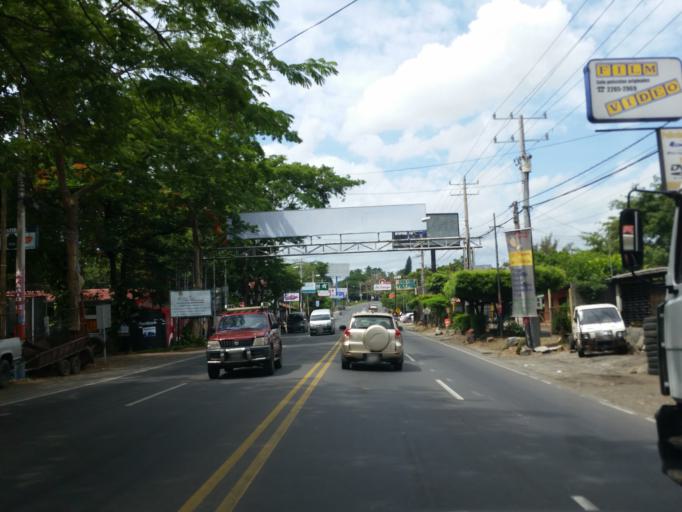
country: NI
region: Managua
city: Ciudad Sandino
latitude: 12.1108
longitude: -86.3161
